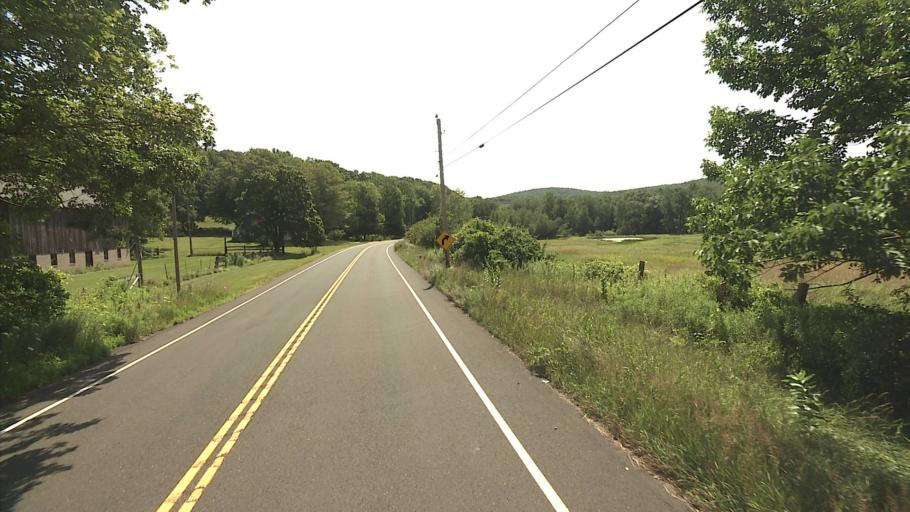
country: US
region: Massachusetts
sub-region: Berkshire County
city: New Marlborough
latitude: 42.0420
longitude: -73.2190
